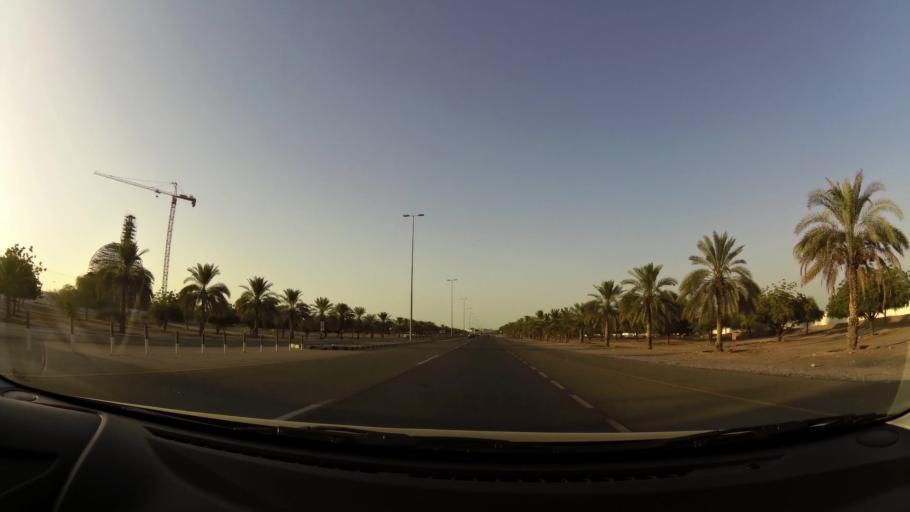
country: OM
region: Muhafazat Masqat
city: As Sib al Jadidah
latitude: 23.5784
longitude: 58.1947
